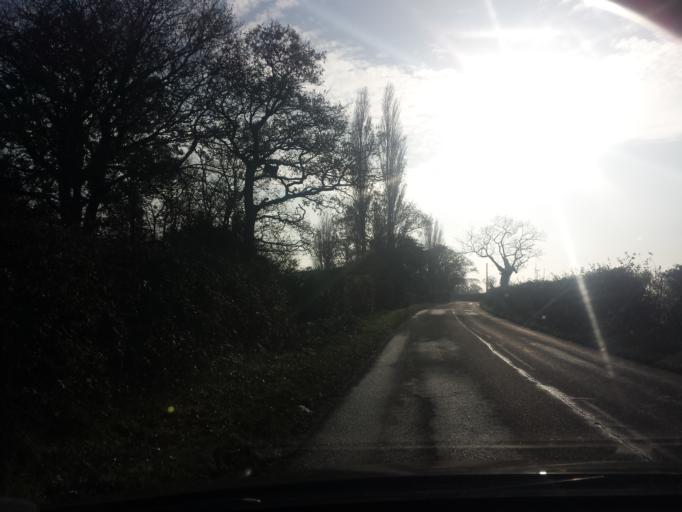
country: GB
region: England
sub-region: Essex
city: Little Clacton
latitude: 51.8285
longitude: 1.1128
